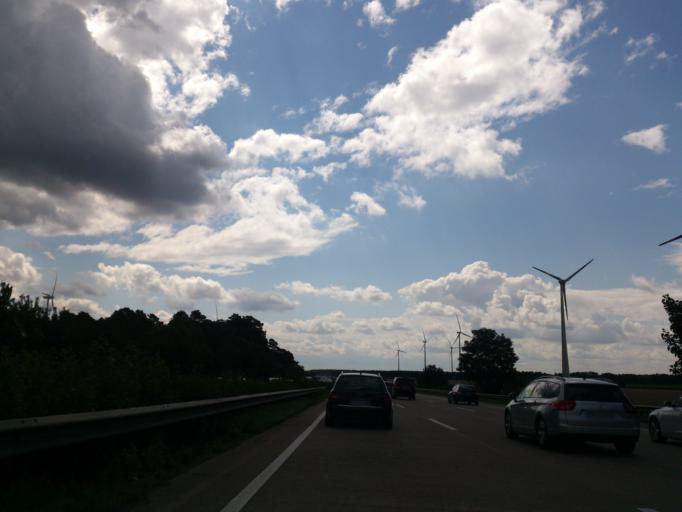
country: DE
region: Lower Saxony
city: Essel
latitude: 52.6630
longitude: 9.6984
